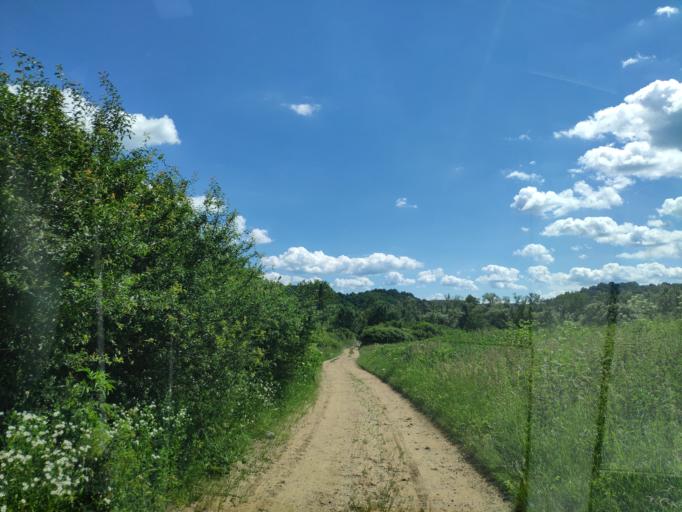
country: HU
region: Borsod-Abauj-Zemplen
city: Arlo
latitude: 48.2715
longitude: 20.1984
